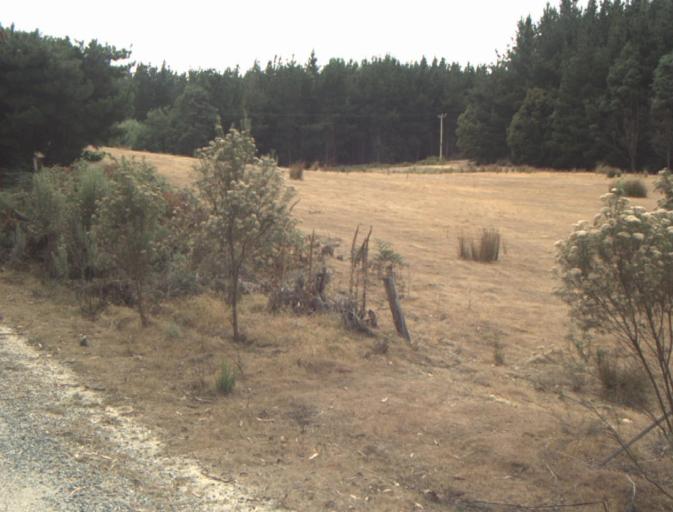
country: AU
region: Tasmania
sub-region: Launceston
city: Mayfield
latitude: -41.1534
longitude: 147.1727
